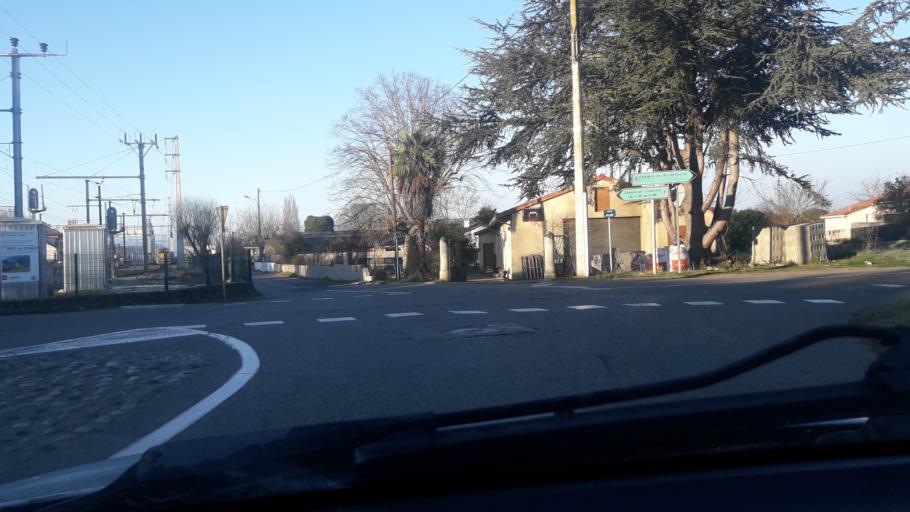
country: FR
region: Midi-Pyrenees
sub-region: Departement de la Haute-Garonne
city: Carbonne
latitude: 43.2999
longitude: 1.2141
